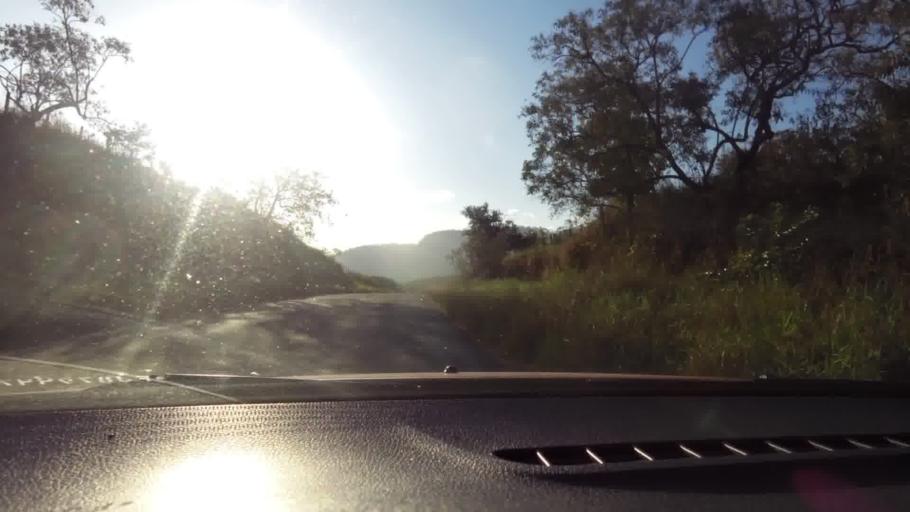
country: BR
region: Espirito Santo
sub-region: Guarapari
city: Guarapari
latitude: -20.5292
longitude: -40.4711
